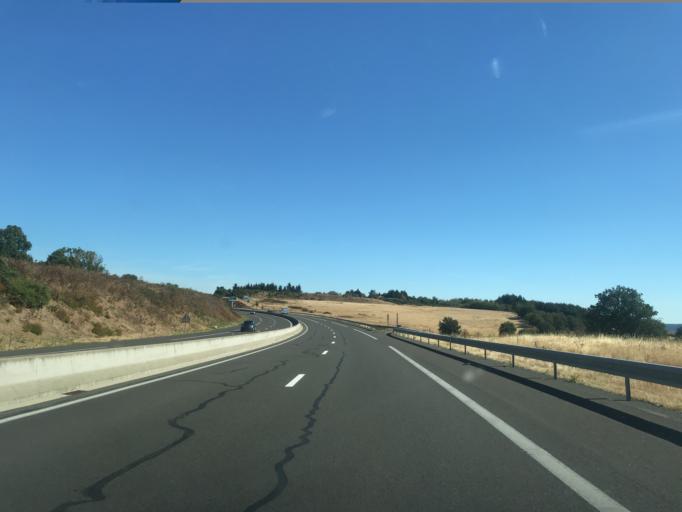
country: FR
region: Auvergne
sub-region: Departement de l'Allier
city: Premilhat
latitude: 46.3274
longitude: 2.5353
